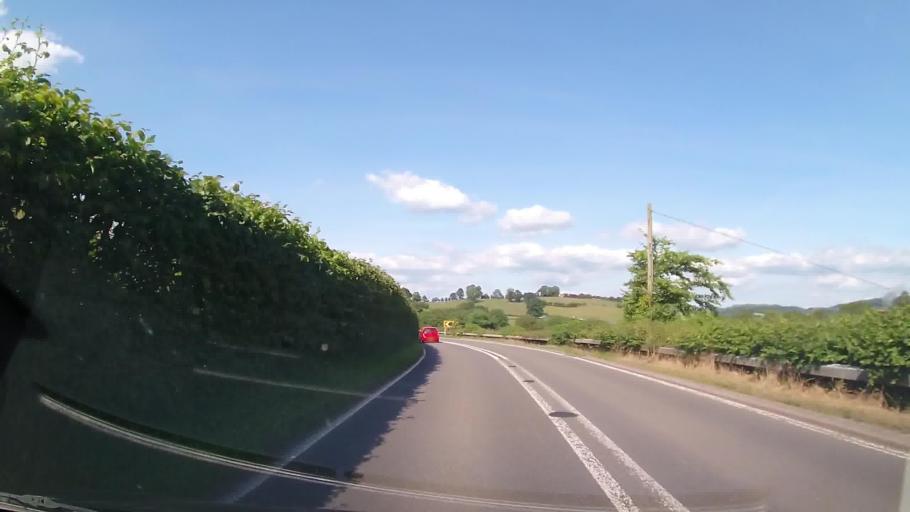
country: GB
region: Wales
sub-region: Sir Powys
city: Llanfyllin
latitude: 52.6629
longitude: -3.3047
